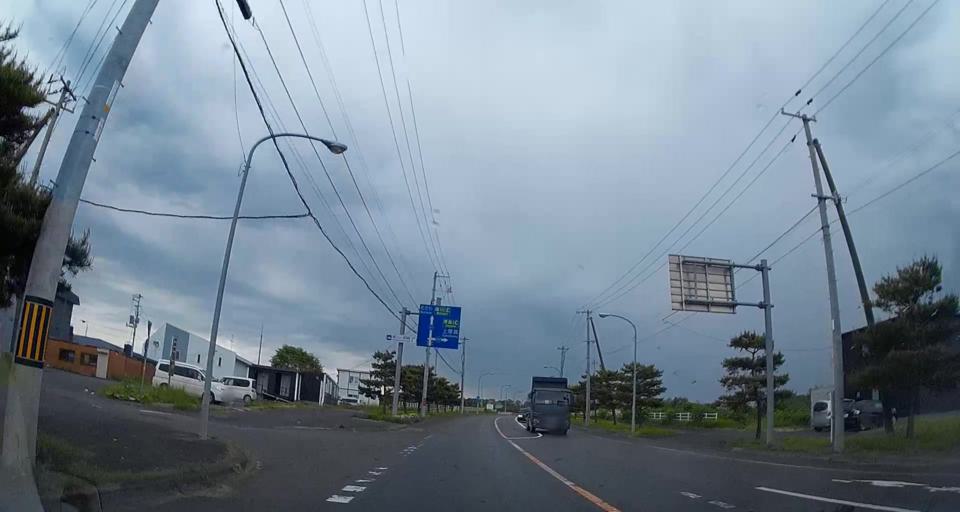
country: JP
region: Hokkaido
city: Chitose
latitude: 42.7227
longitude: 141.8755
